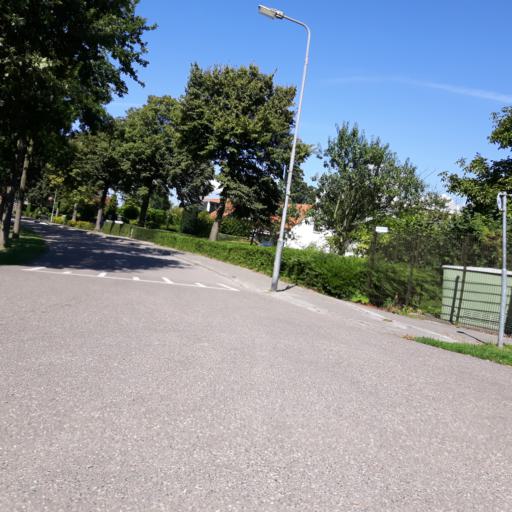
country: NL
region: Zeeland
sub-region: Schouwen-Duiveland
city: Bruinisse
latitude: 51.6234
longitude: 3.9856
